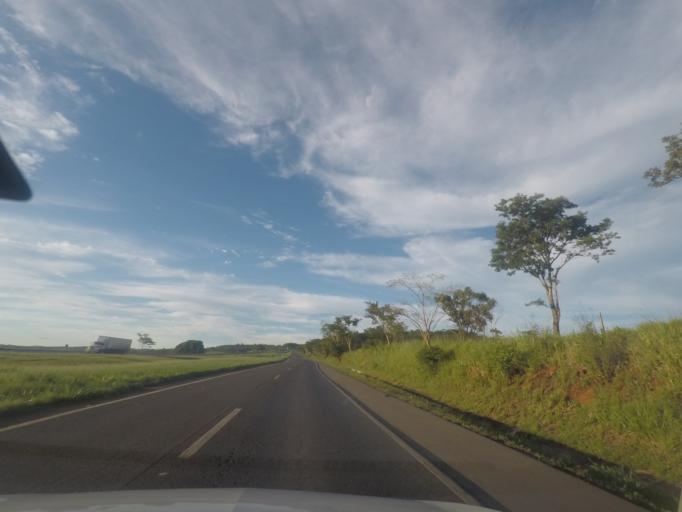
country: BR
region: Goias
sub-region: Goiatuba
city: Goiatuba
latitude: -18.0849
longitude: -49.2704
